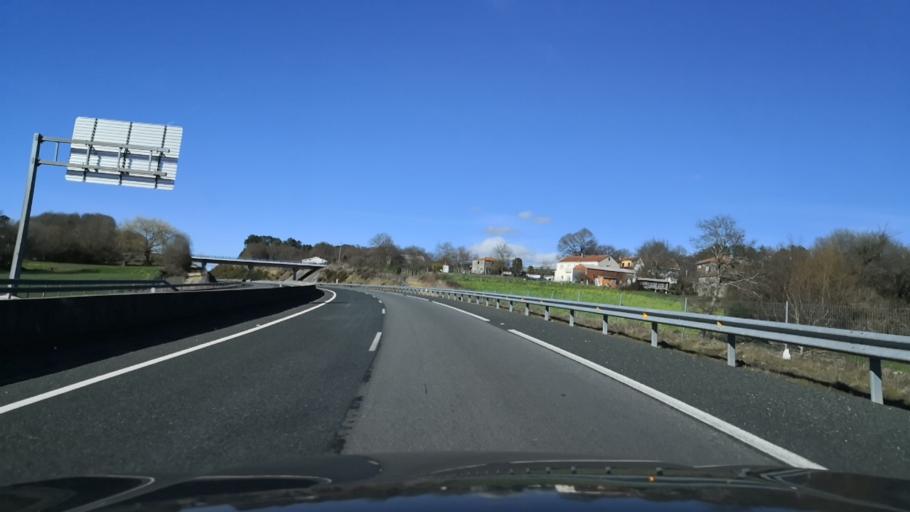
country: ES
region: Galicia
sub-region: Provincia de Pontevedra
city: Lalin
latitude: 42.6467
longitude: -8.1330
